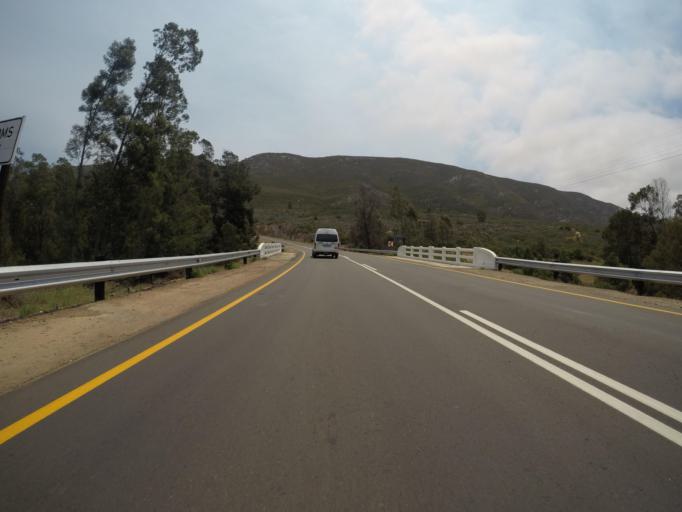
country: ZA
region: Western Cape
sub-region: Eden District Municipality
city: Knysna
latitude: -33.7628
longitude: 22.9628
